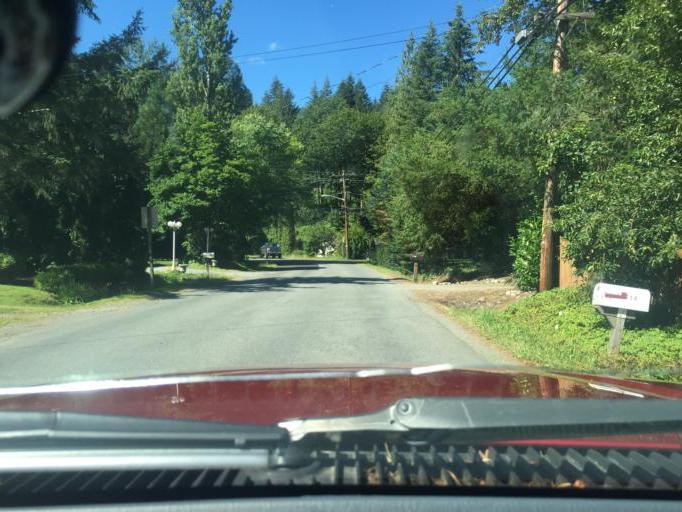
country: US
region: Washington
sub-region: King County
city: Riverbend
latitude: 47.4655
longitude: -121.7566
